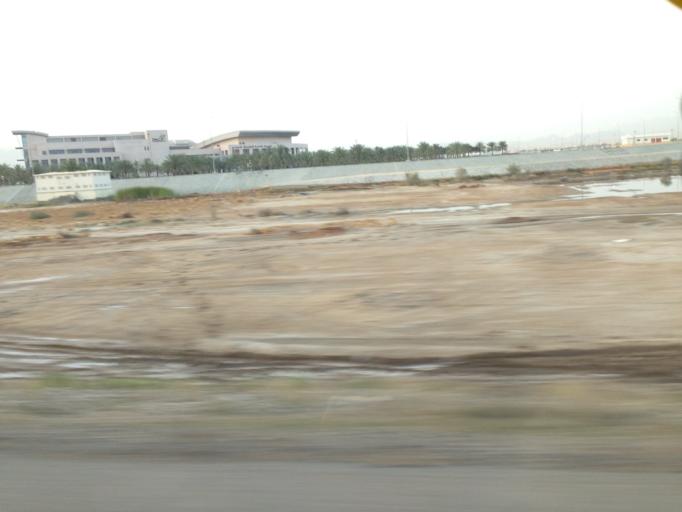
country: OM
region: Muhafazat Masqat
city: As Sib al Jadidah
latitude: 23.6241
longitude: 58.2655
